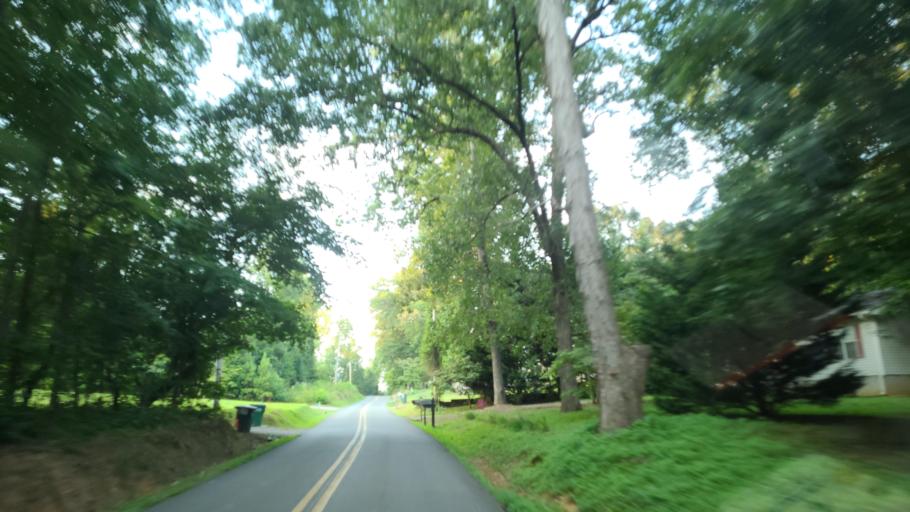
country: US
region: Georgia
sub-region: Bartow County
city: Adairsville
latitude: 34.4276
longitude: -84.9069
